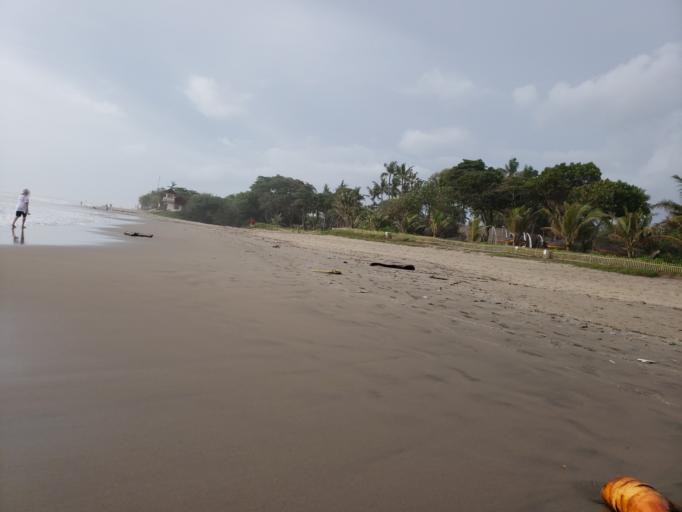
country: ID
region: Bali
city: Kuta
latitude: -8.6899
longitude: 115.1562
